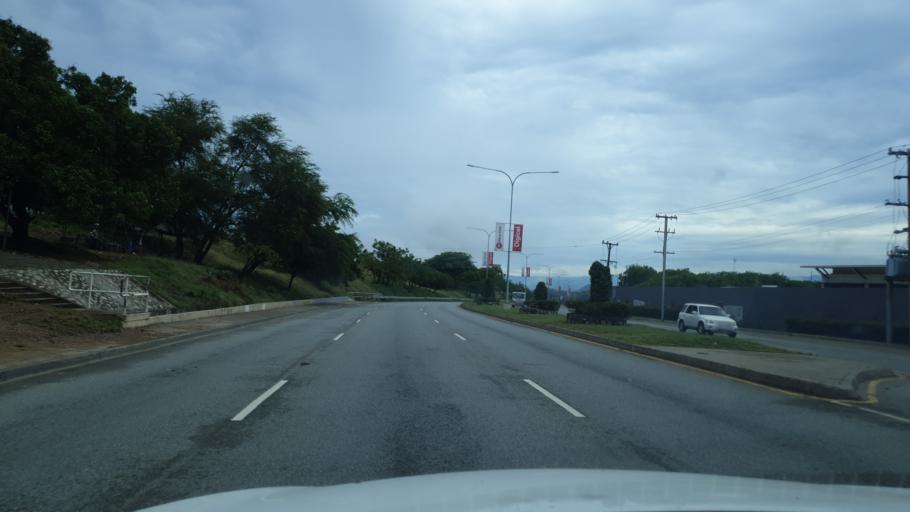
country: PG
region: National Capital
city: Port Moresby
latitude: -9.4322
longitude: 147.1792
